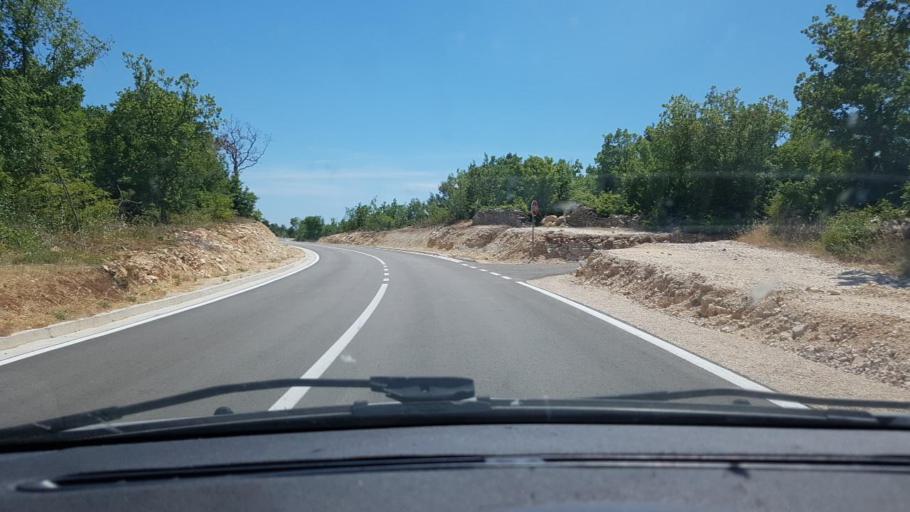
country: HR
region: Sibensko-Kniniska
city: Kistanje
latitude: 43.8799
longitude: 15.9137
